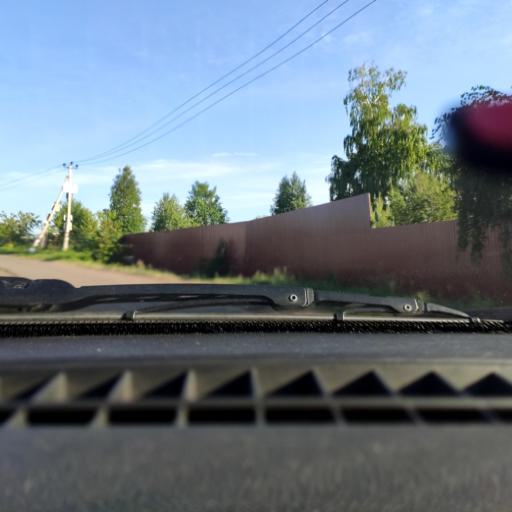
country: RU
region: Bashkortostan
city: Avdon
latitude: 54.4601
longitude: 55.8480
